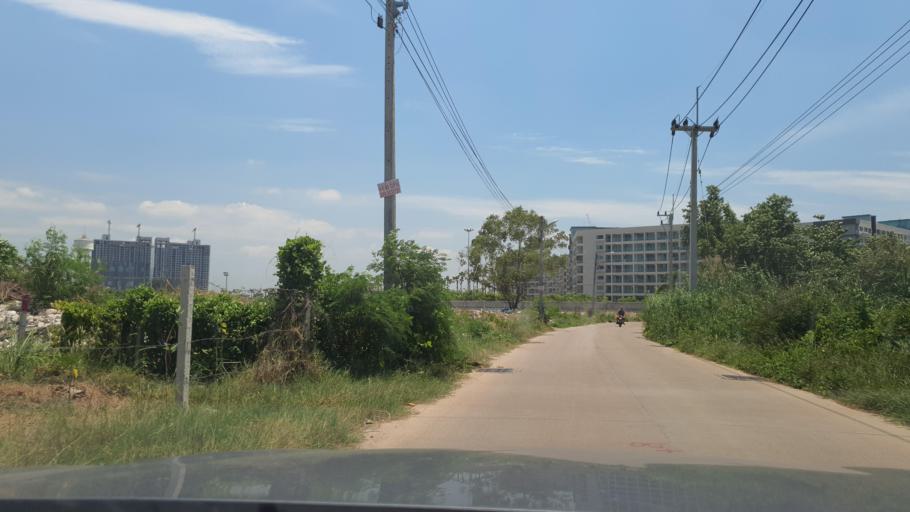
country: TH
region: Chon Buri
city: Phatthaya
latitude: 12.8978
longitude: 100.8828
